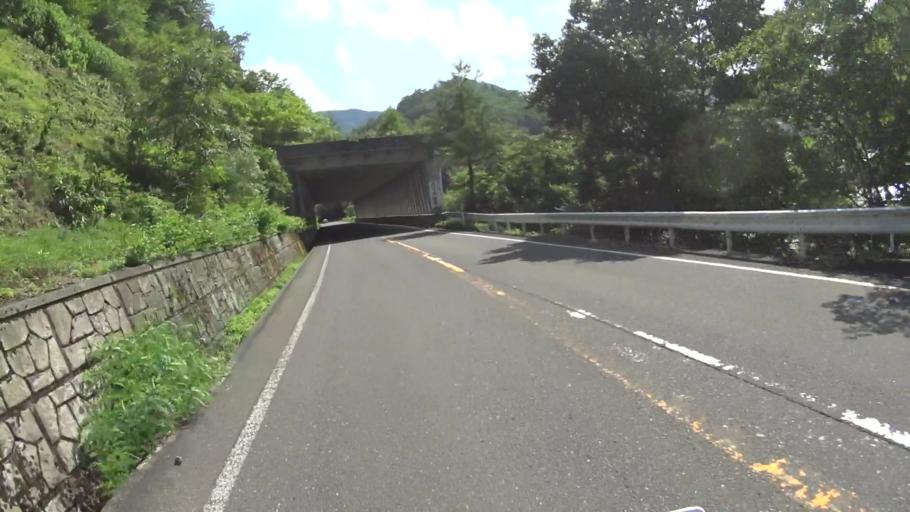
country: JP
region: Fukui
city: Obama
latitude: 35.3942
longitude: 135.5835
